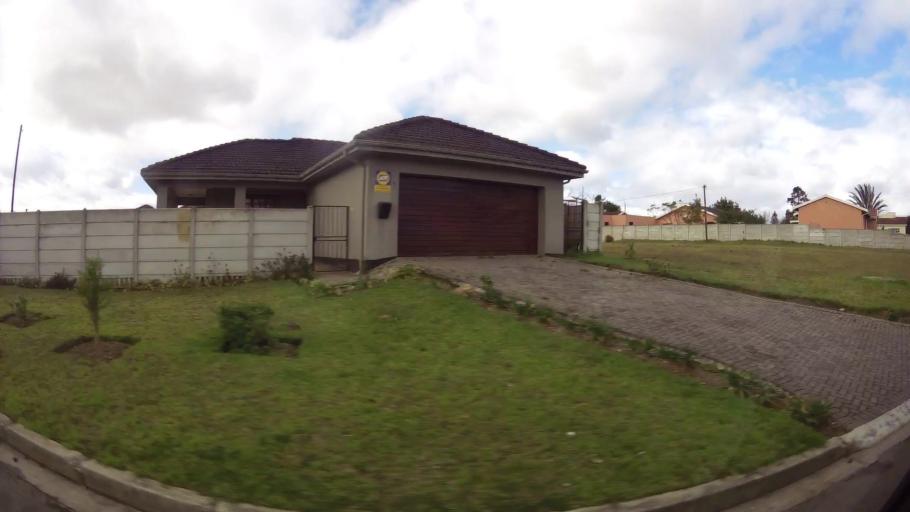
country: ZA
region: Western Cape
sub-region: Eden District Municipality
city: George
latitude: -34.0067
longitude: 22.4428
